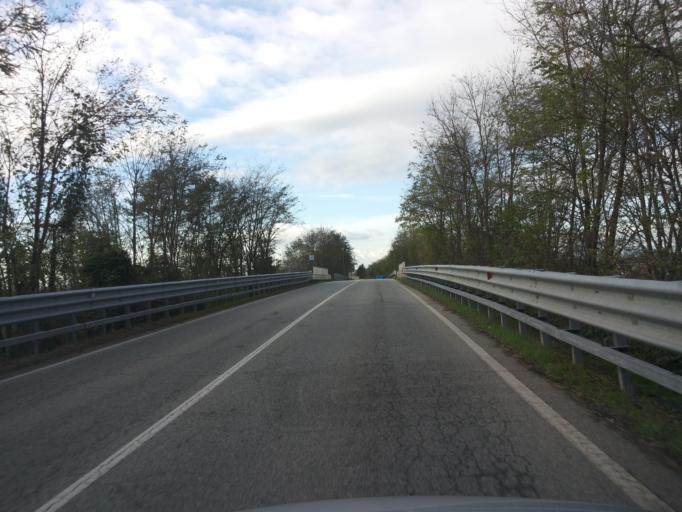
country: IT
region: Piedmont
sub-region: Provincia di Vercelli
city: Tronzano Vercellese
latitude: 45.3403
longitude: 8.1671
